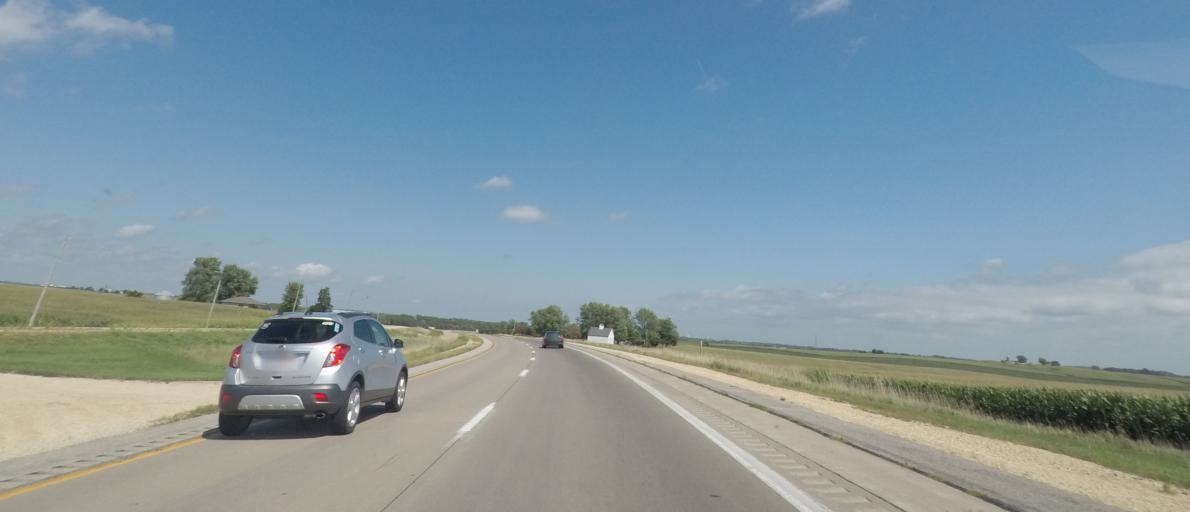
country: US
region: Iowa
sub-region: Linn County
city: Springville
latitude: 42.0410
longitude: -91.5163
